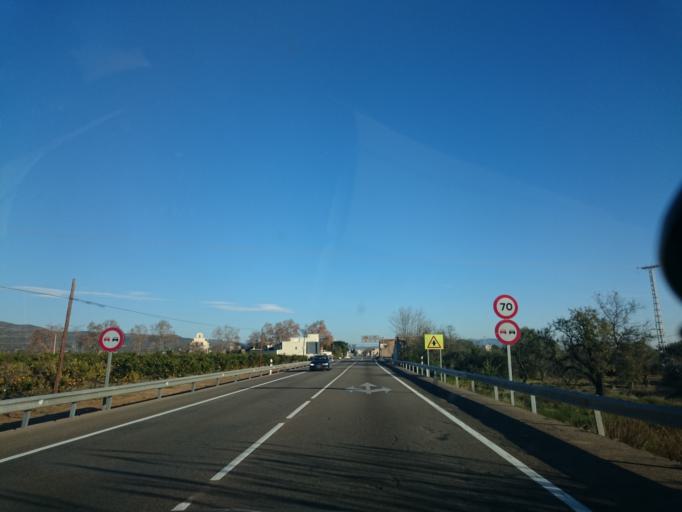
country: ES
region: Valencia
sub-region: Provincia de Castello
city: Orpesa/Oropesa del Mar
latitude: 40.1370
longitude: 0.1505
